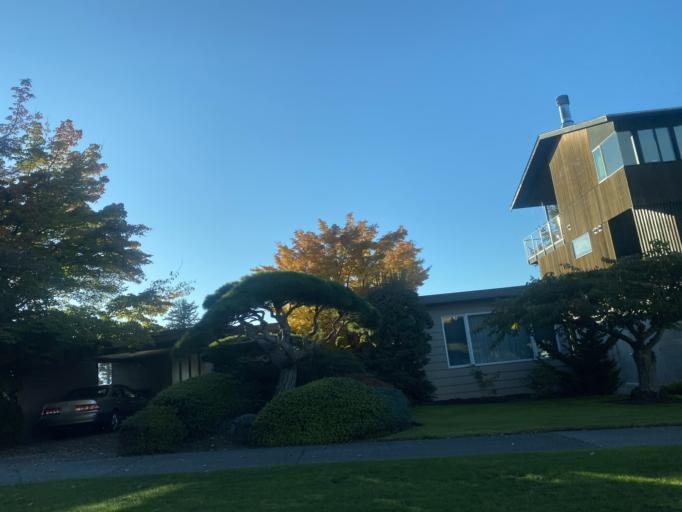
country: US
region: Washington
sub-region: King County
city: Seattle
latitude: 47.6480
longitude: -122.4120
